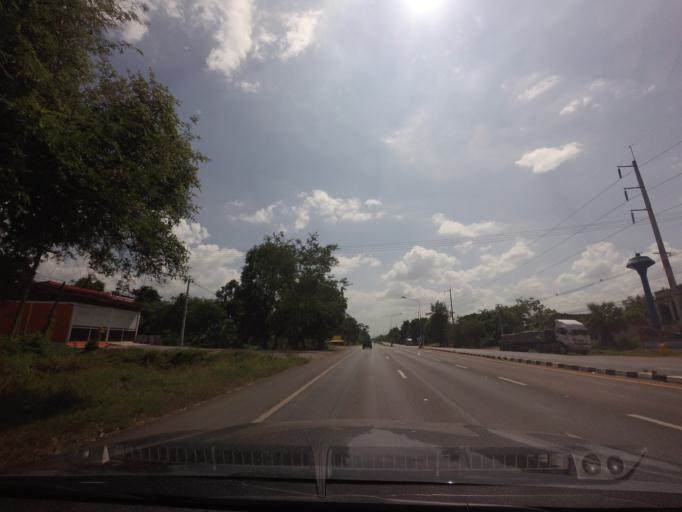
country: TH
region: Phetchabun
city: Nong Phai
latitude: 15.8912
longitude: 101.0237
